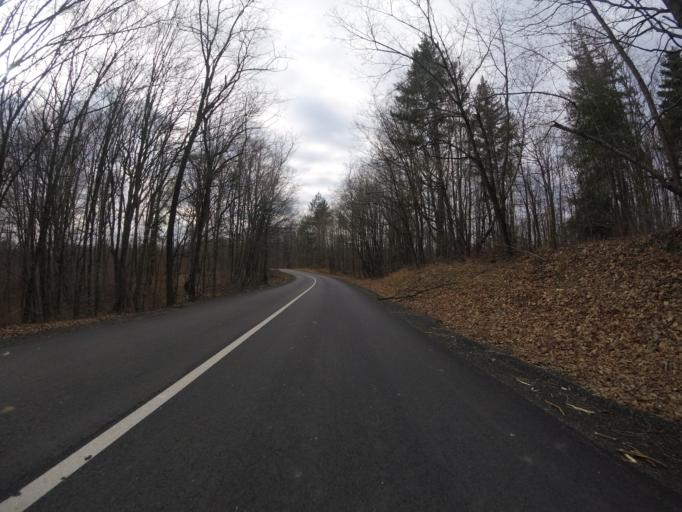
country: HR
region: Zagrebacka
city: Mraclin
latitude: 45.5316
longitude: 16.0565
